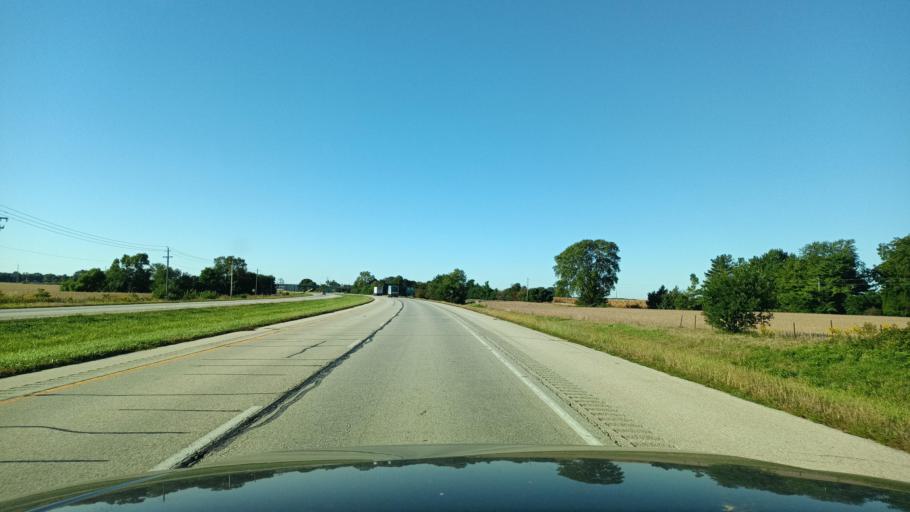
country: US
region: Illinois
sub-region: Knox County
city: Galesburg
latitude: 40.9687
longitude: -90.4007
